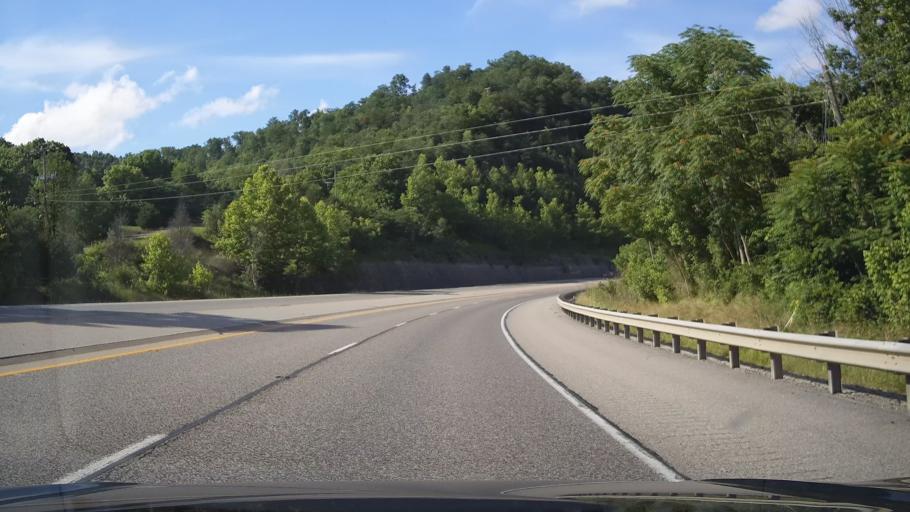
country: US
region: Kentucky
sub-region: Lawrence County
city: Louisa
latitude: 38.0087
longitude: -82.6651
